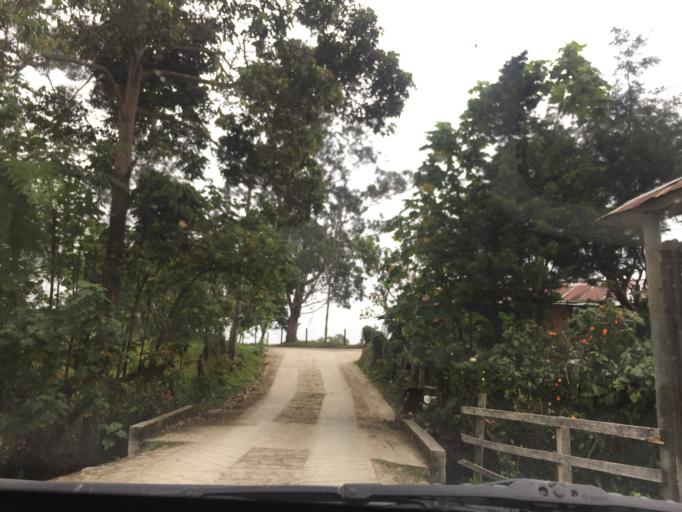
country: CO
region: Cundinamarca
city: Bojaca
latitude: 4.6932
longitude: -74.3729
